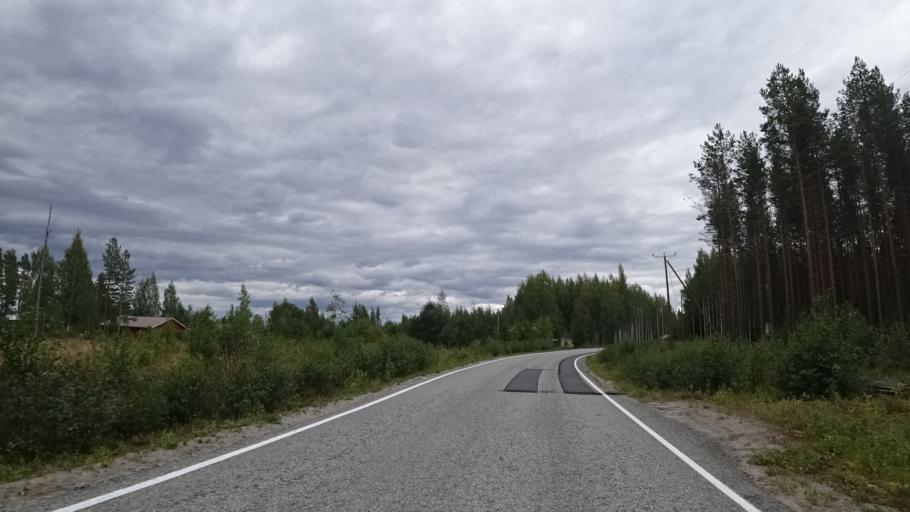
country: FI
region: North Karelia
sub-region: Joensuu
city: Ilomantsi
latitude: 62.4551
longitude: 31.1125
